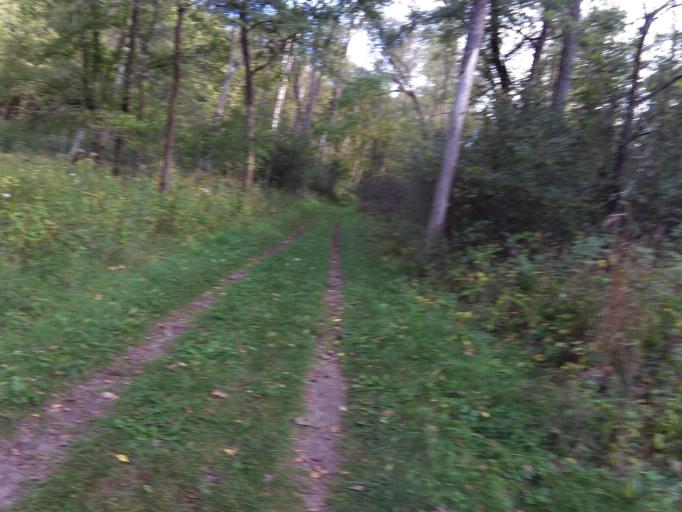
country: US
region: Minnesota
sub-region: Washington County
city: Afton
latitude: 44.8612
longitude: -92.7940
